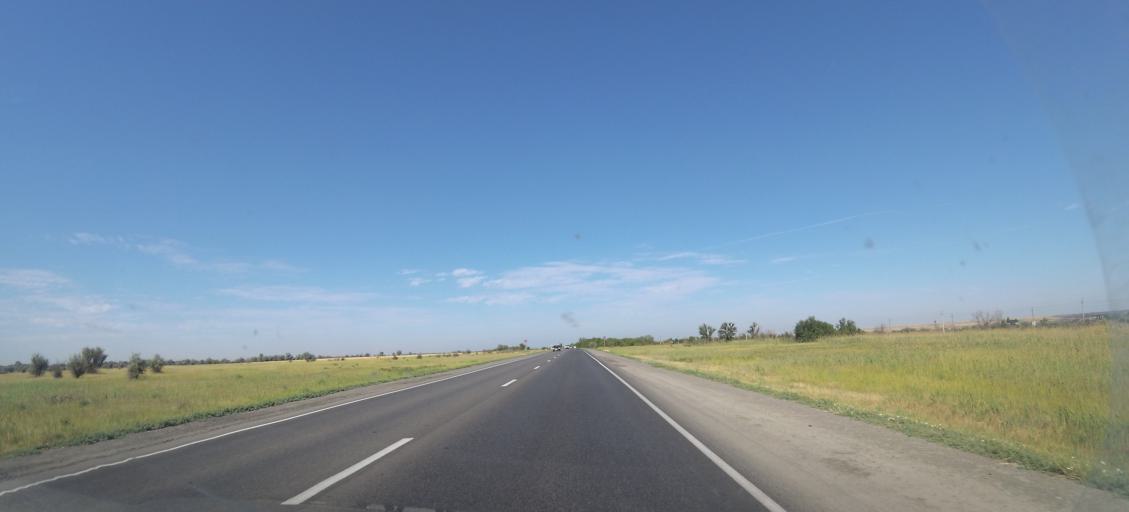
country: RU
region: Volgograd
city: Novyy Rogachik
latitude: 48.6860
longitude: 43.9446
